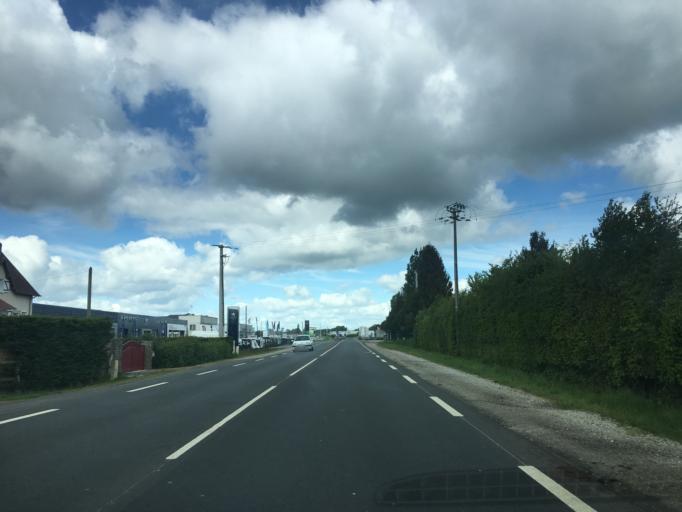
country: FR
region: Lower Normandy
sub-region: Departement de l'Orne
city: Saint-Sulpice-sur-Risle
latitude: 48.7601
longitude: 0.6697
